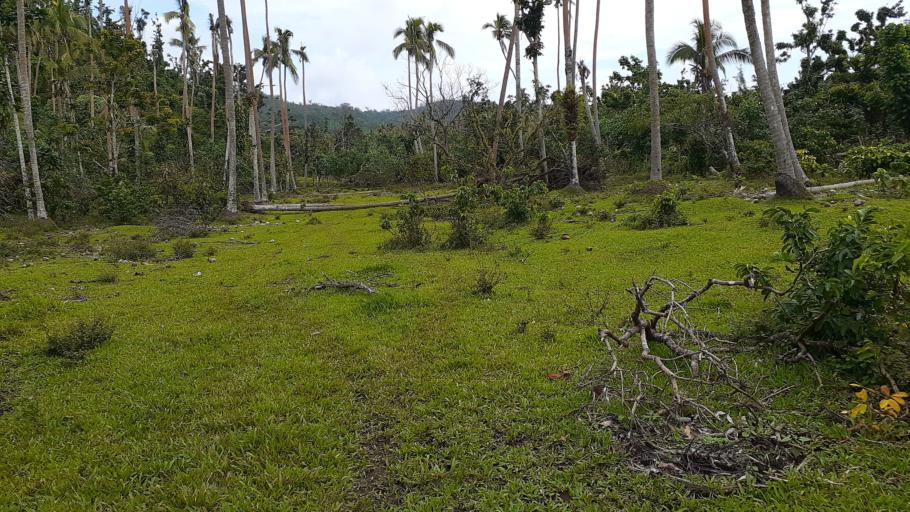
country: VU
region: Penama
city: Saratamata
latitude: -15.9496
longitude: 168.1954
